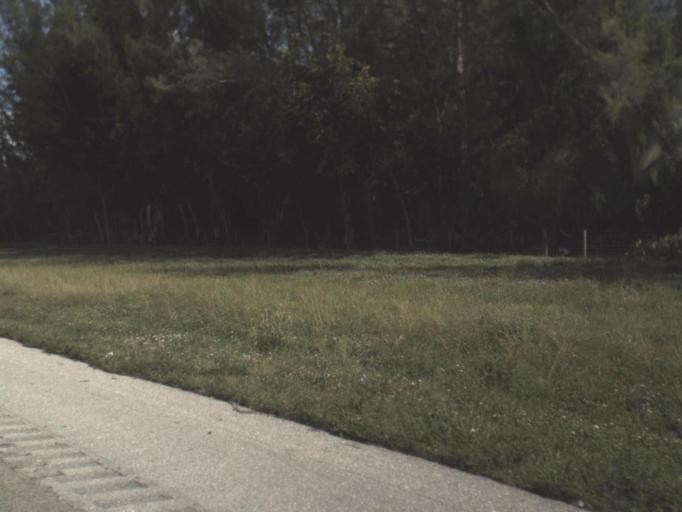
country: US
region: Florida
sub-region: Palm Beach County
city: Villages of Oriole
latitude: 26.4444
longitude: -80.1742
